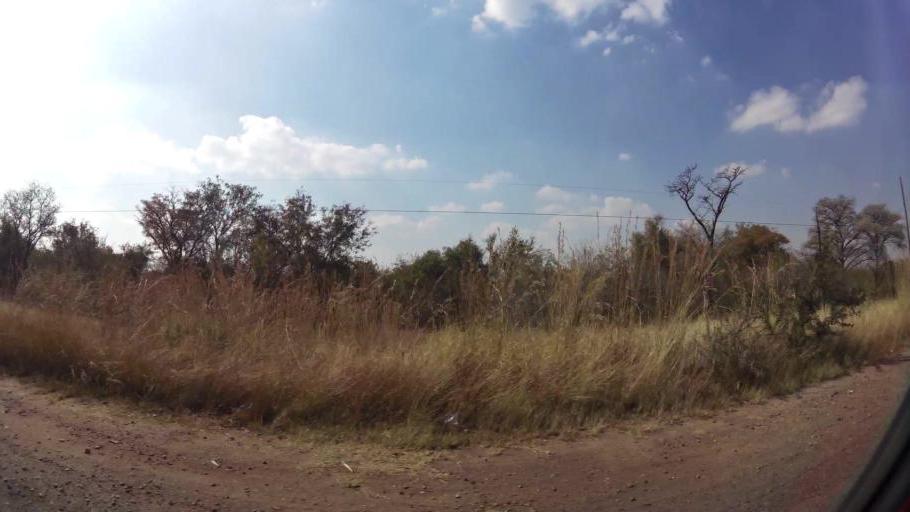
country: ZA
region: North-West
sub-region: Bojanala Platinum District Municipality
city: Rustenburg
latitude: -25.5231
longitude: 27.1081
